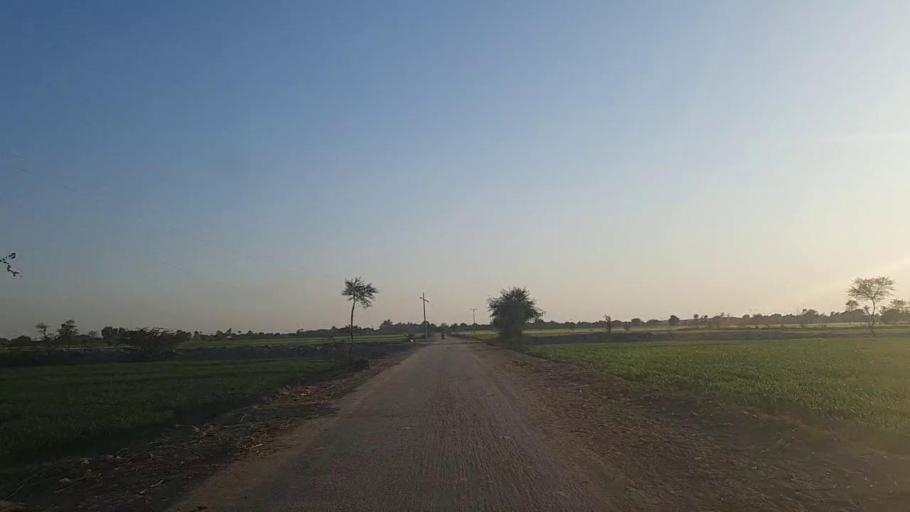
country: PK
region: Sindh
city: Jam Sahib
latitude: 26.3290
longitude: 68.6974
